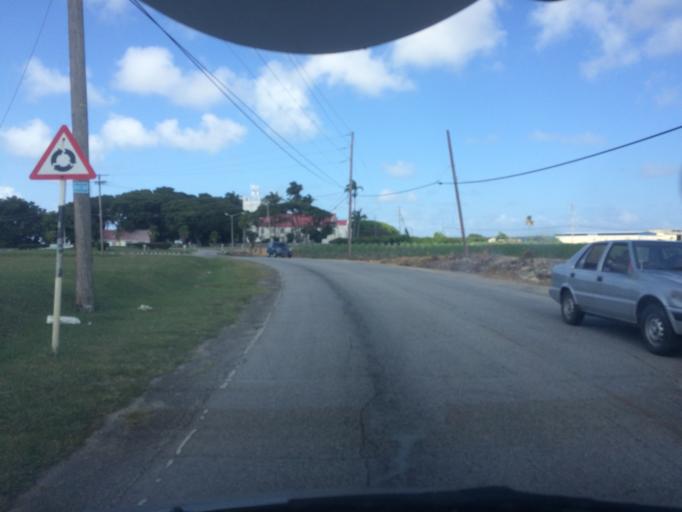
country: BB
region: Saint Lucy
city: Checker Hall
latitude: 13.2904
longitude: -59.6229
